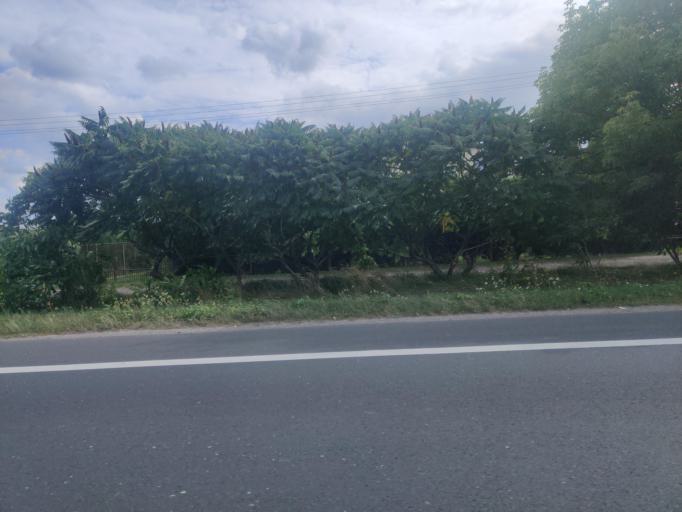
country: PL
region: Greater Poland Voivodeship
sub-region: Powiat koninski
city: Stare Miasto
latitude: 52.1892
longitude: 18.2447
